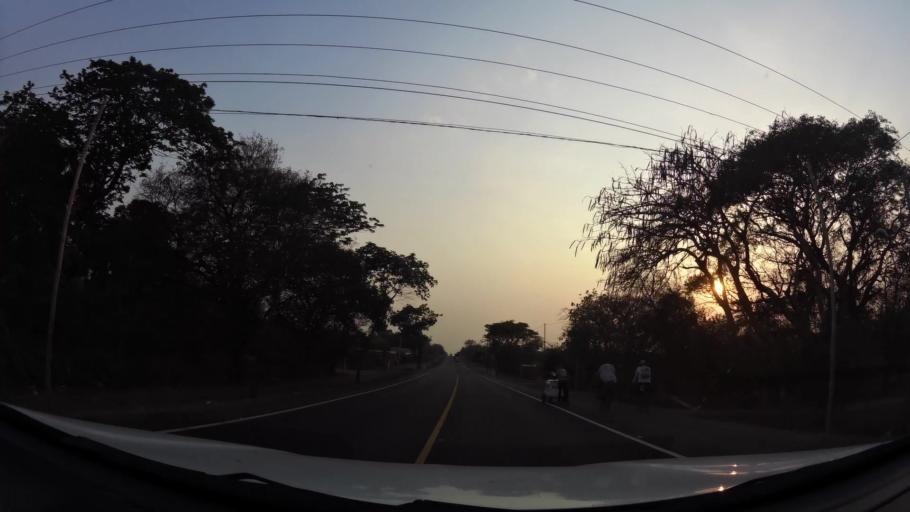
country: NI
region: Leon
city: La Paz Centro
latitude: 12.3376
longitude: -86.6622
